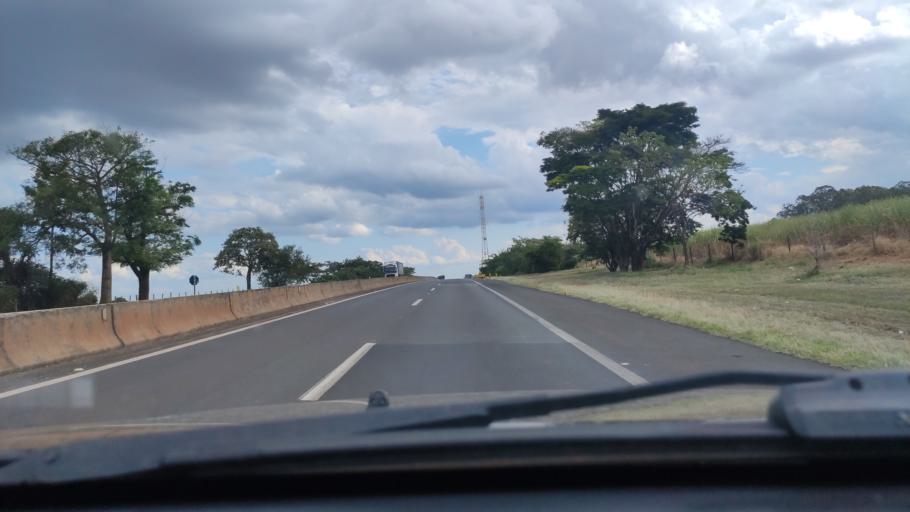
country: BR
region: Sao Paulo
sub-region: Santa Cruz Do Rio Pardo
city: Santa Cruz do Rio Pardo
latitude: -22.8218
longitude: -49.5482
